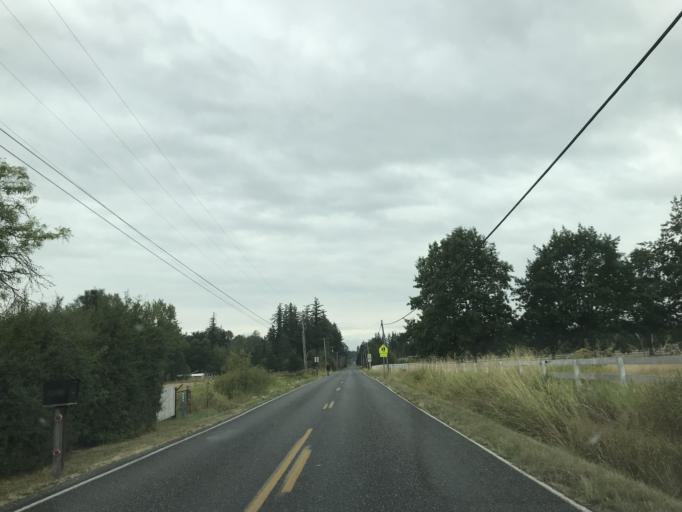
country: US
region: Washington
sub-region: Whatcom County
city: Sudden Valley
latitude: 48.8201
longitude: -122.3325
